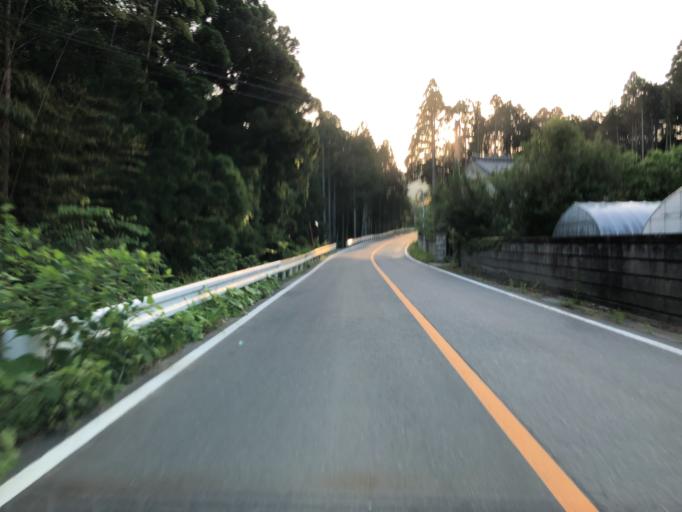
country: JP
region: Fukushima
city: Iwaki
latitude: 37.2204
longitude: 140.9702
